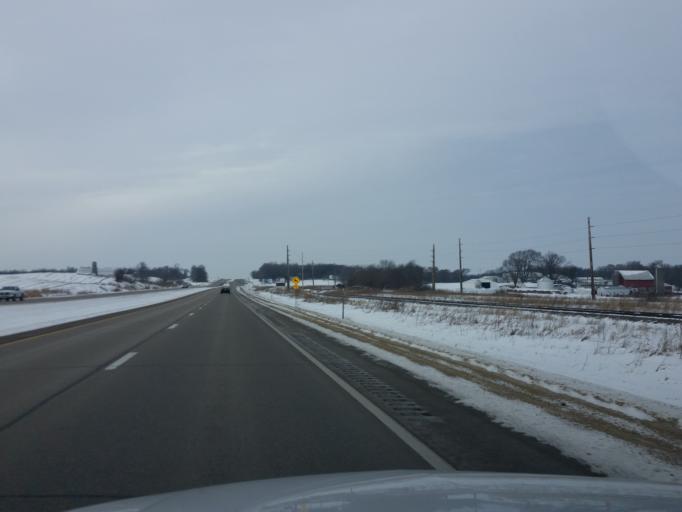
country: US
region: Iowa
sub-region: Dubuque County
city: Dyersville
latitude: 42.4632
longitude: -91.0679
